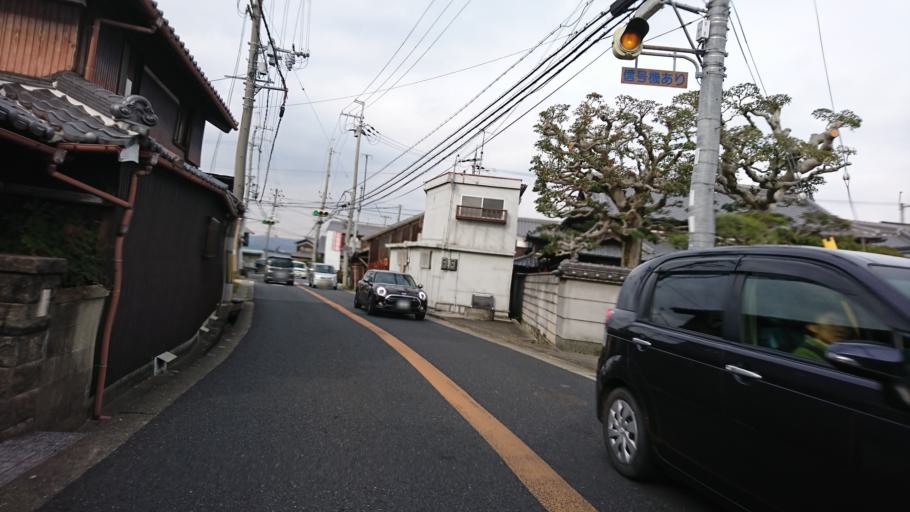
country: JP
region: Hyogo
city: Kakogawacho-honmachi
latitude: 34.7781
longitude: 134.8768
